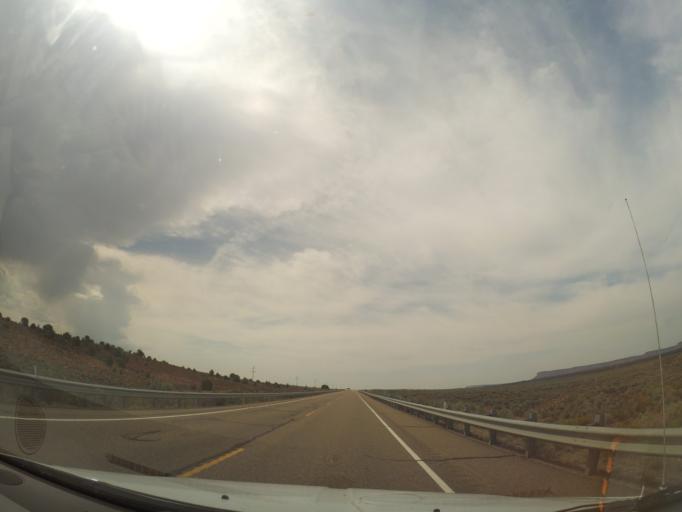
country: US
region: Utah
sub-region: Kane County
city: Kanab
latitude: 37.1298
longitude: -112.0917
